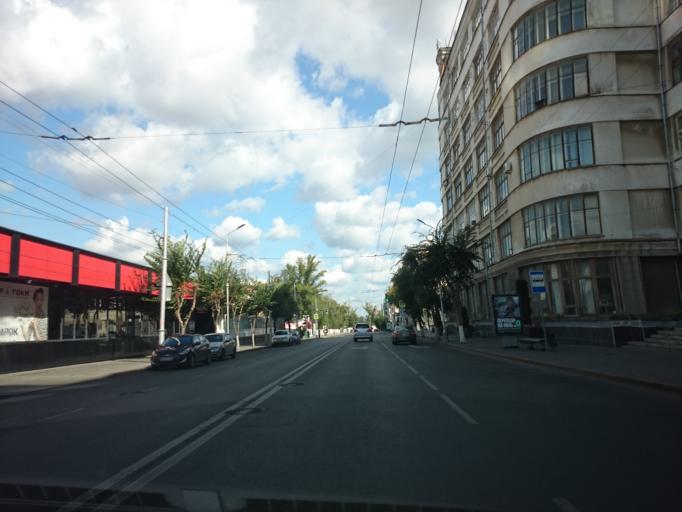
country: RU
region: Samara
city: Rozhdestveno
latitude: 53.1942
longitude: 50.0933
